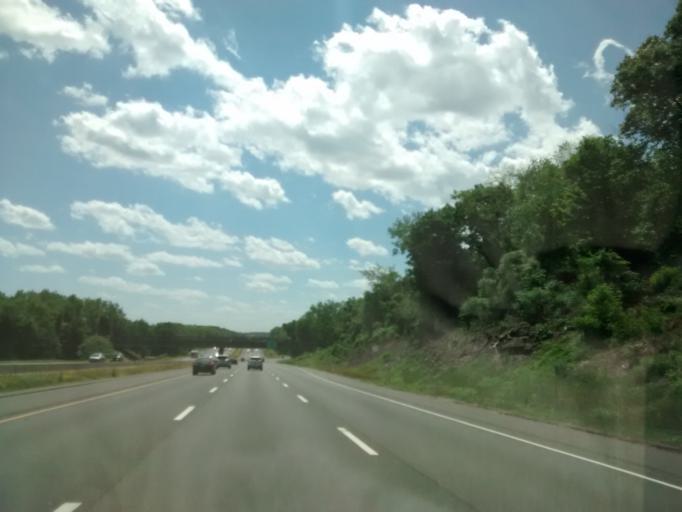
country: US
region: Connecticut
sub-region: Tolland County
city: Rockville
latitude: 41.8369
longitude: -72.4583
